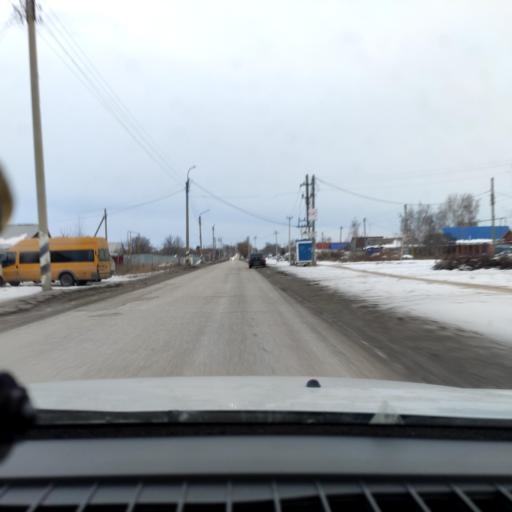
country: RU
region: Samara
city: Chapayevsk
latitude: 52.9942
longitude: 49.7142
